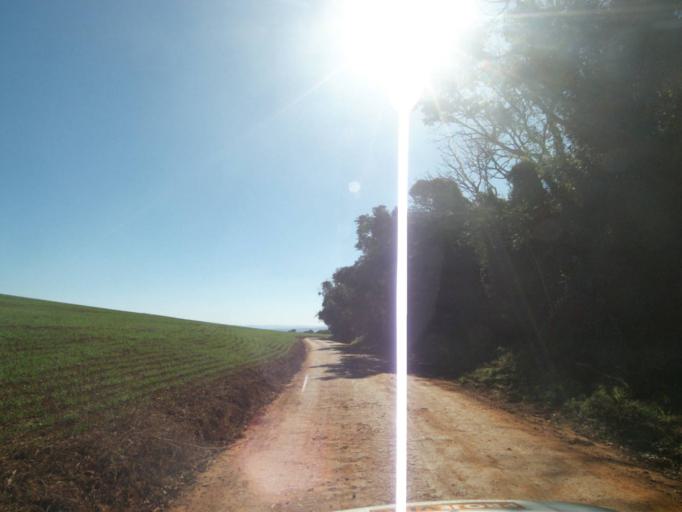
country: BR
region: Parana
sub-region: Tibagi
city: Tibagi
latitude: -24.5696
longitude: -50.6267
